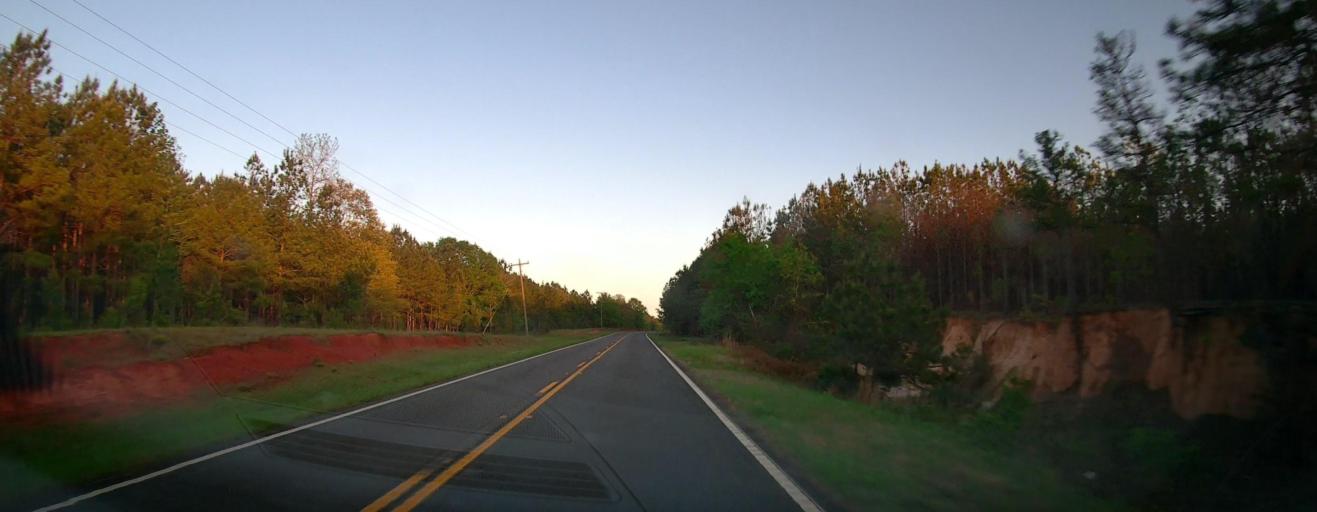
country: US
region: Georgia
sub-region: Marion County
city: Buena Vista
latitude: 32.3912
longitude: -84.5685
